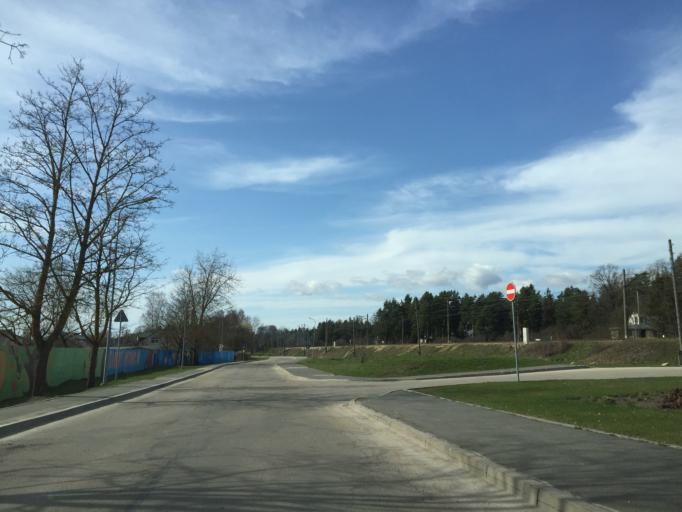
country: LV
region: Ogre
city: Ogre
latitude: 56.8186
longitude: 24.5920
